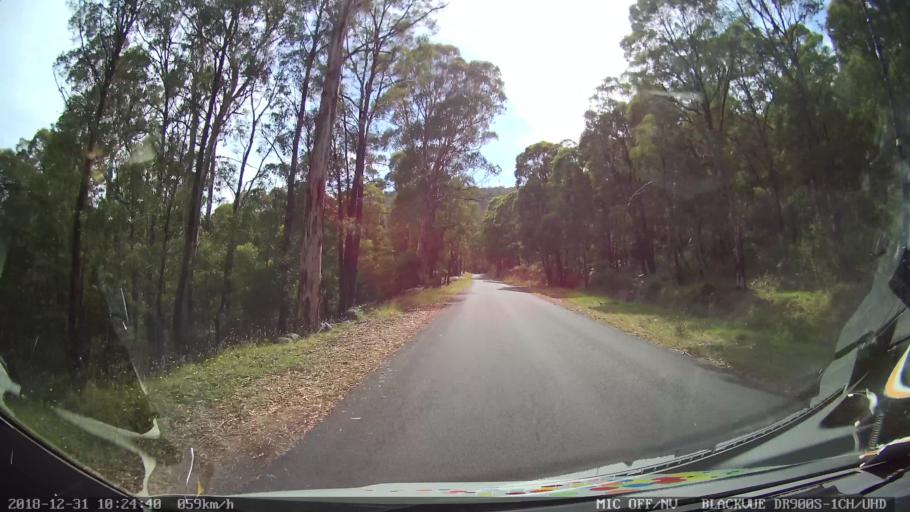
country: AU
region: New South Wales
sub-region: Snowy River
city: Jindabyne
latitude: -36.5114
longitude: 148.1421
